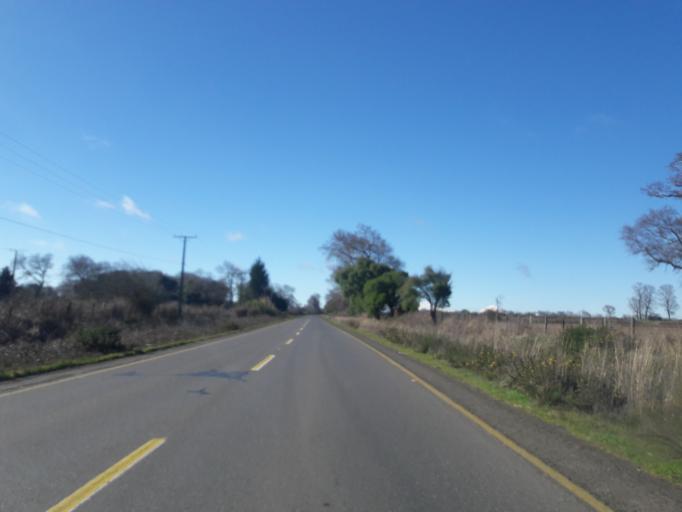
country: CL
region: Araucania
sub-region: Provincia de Malleco
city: Victoria
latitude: -38.2537
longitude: -72.2883
